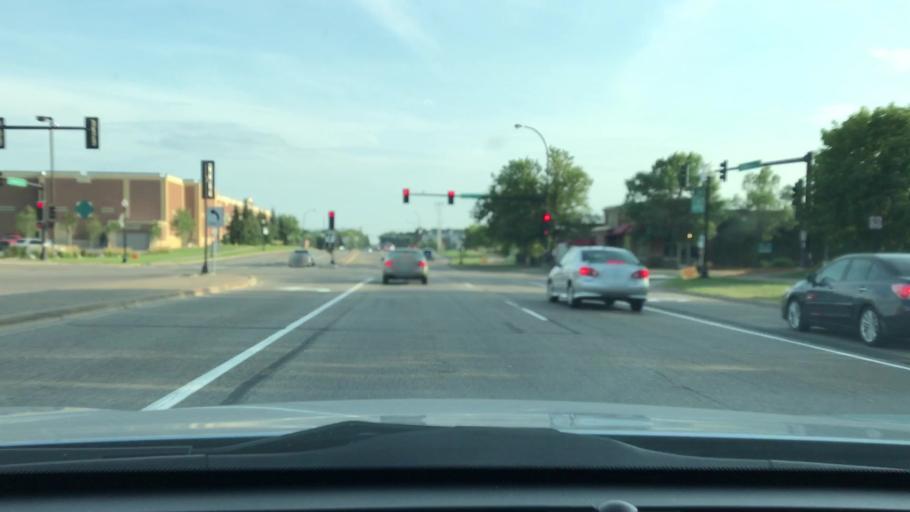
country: US
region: Minnesota
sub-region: Hennepin County
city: Plymouth
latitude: 45.0213
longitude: -93.4818
